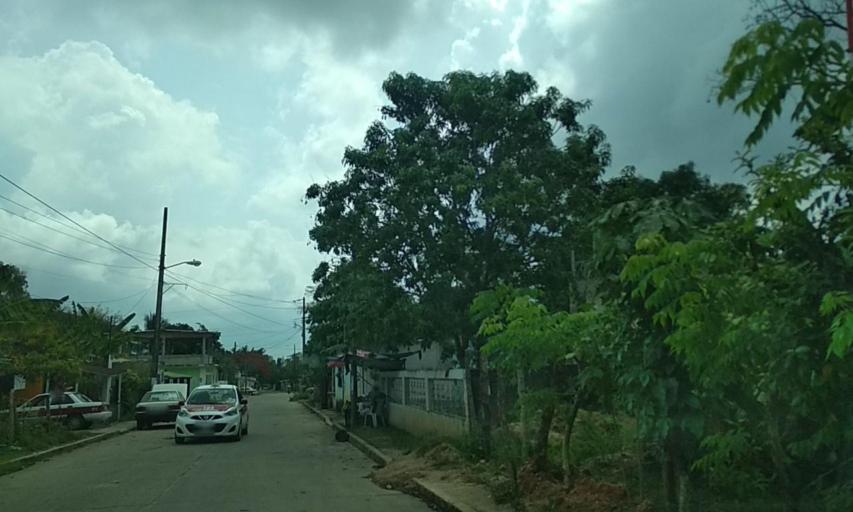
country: MX
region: Veracruz
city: Las Choapas
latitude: 17.9014
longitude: -94.1061
